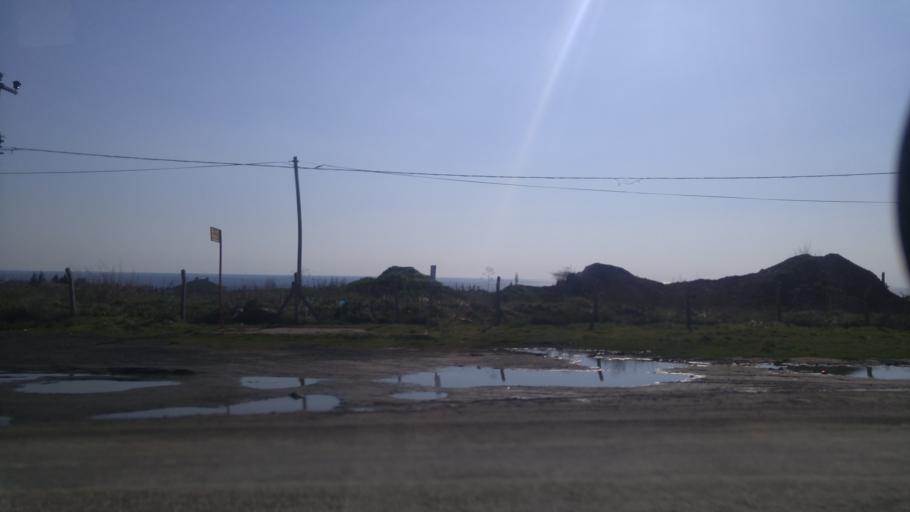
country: TR
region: Istanbul
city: Kavakli
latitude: 41.0687
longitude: 28.2937
